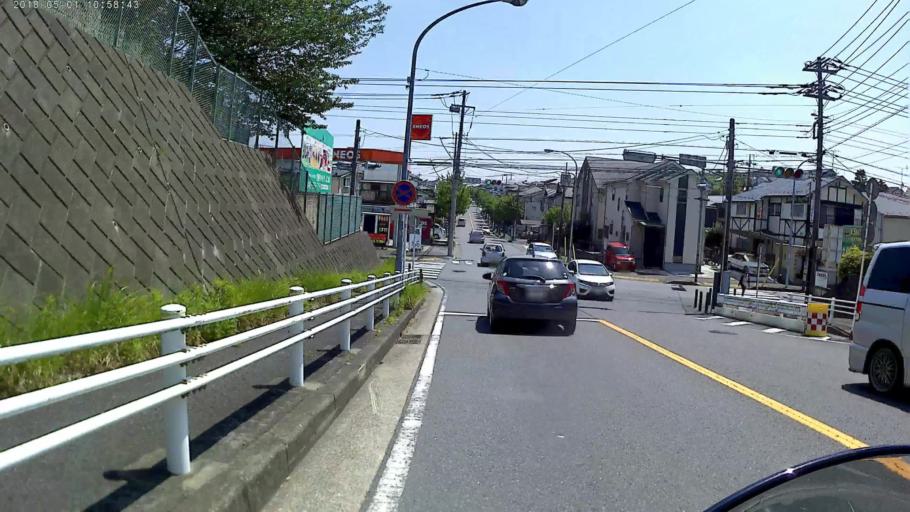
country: JP
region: Kanagawa
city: Minami-rinkan
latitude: 35.4789
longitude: 139.5111
